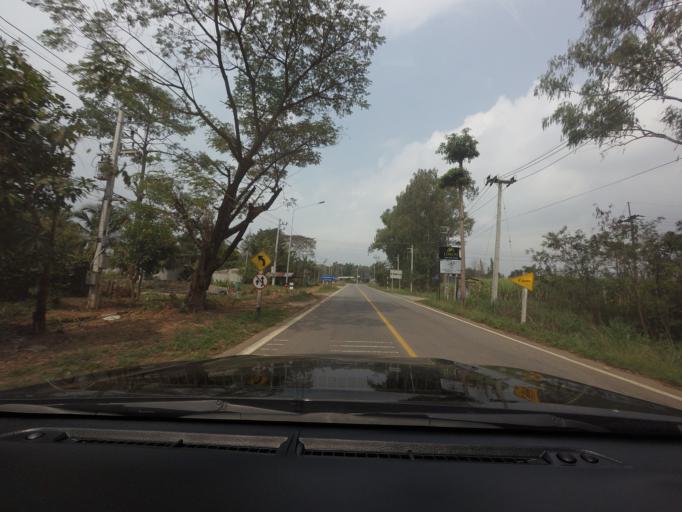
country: TH
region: Nakhon Ratchasima
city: Pak Chong
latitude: 14.4892
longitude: 101.5568
